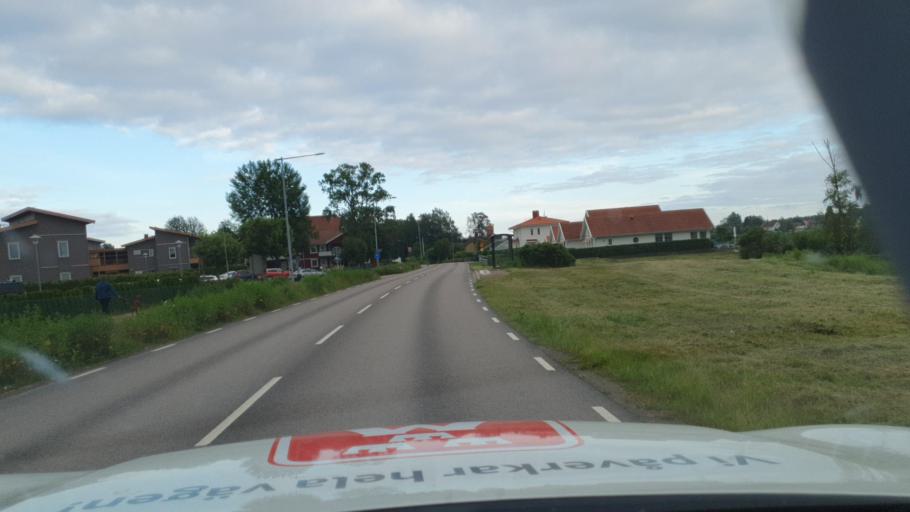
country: SE
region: Vaermland
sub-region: Karlstads Kommun
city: Karlstad
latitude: 59.4147
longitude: 13.4920
